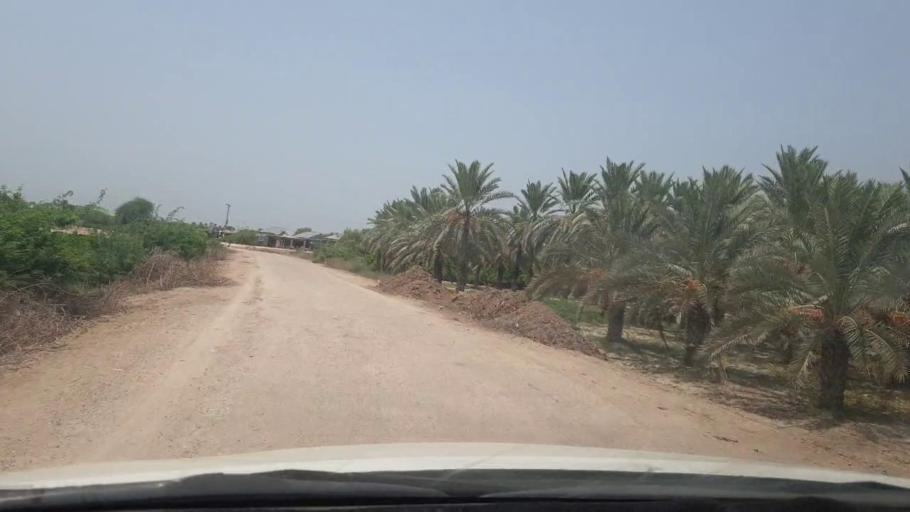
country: PK
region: Sindh
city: Khairpur
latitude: 27.5064
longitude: 68.8600
